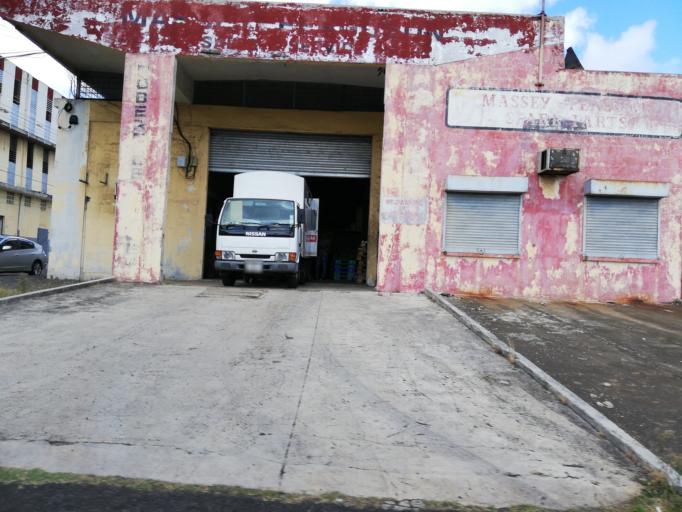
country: MU
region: Black River
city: Petite Riviere
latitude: -20.1900
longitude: 57.4668
